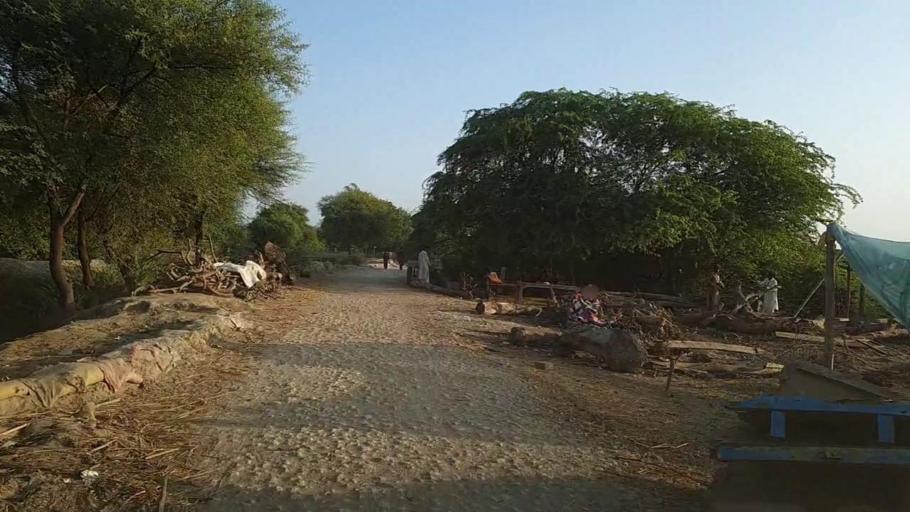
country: PK
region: Sindh
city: Kario
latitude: 24.6912
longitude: 68.6728
